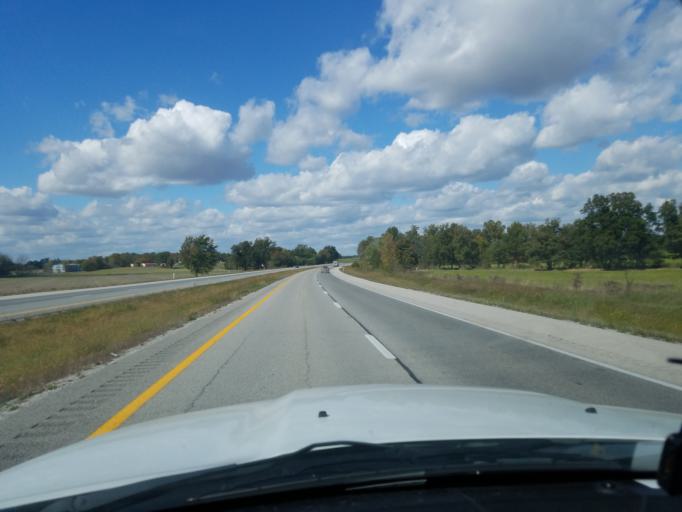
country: US
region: Kentucky
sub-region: Daviess County
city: Masonville
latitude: 37.6655
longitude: -87.0194
